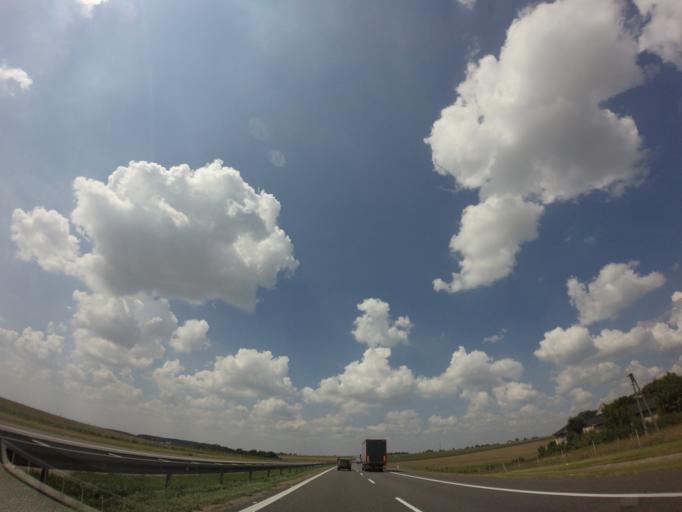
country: PL
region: Opole Voivodeship
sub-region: Powiat krapkowicki
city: Gogolin
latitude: 50.4787
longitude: 18.0671
